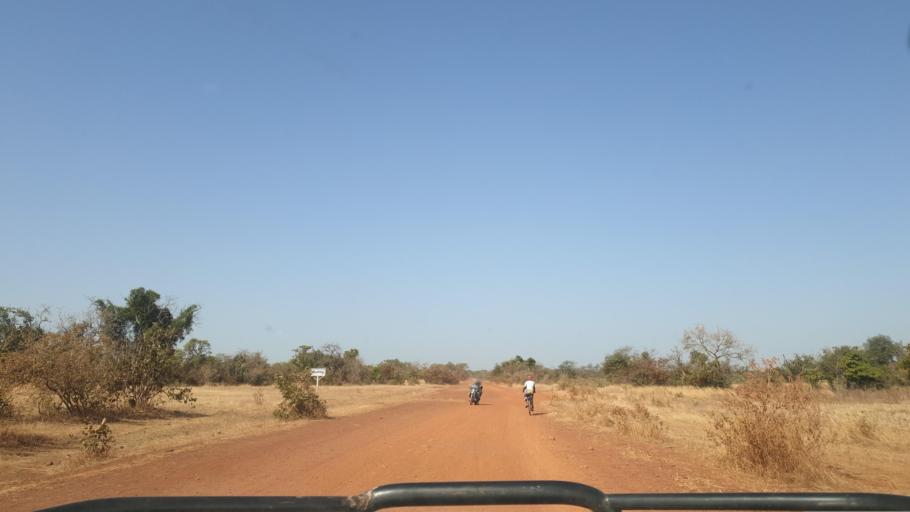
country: ML
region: Sikasso
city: Bougouni
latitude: 11.8178
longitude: -6.9406
